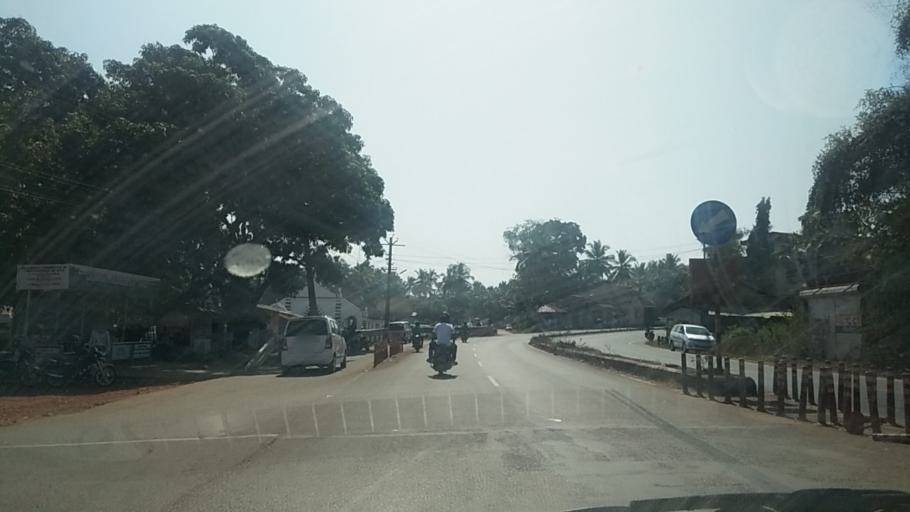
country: IN
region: Goa
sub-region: South Goa
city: Raia
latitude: 15.3137
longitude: 73.9838
